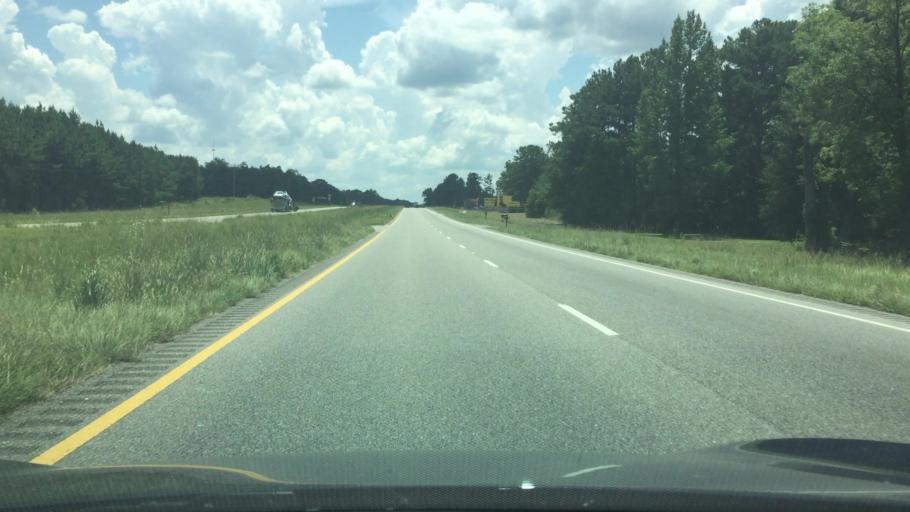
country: US
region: Alabama
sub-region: Montgomery County
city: Taylor
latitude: 32.0561
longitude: -86.0476
